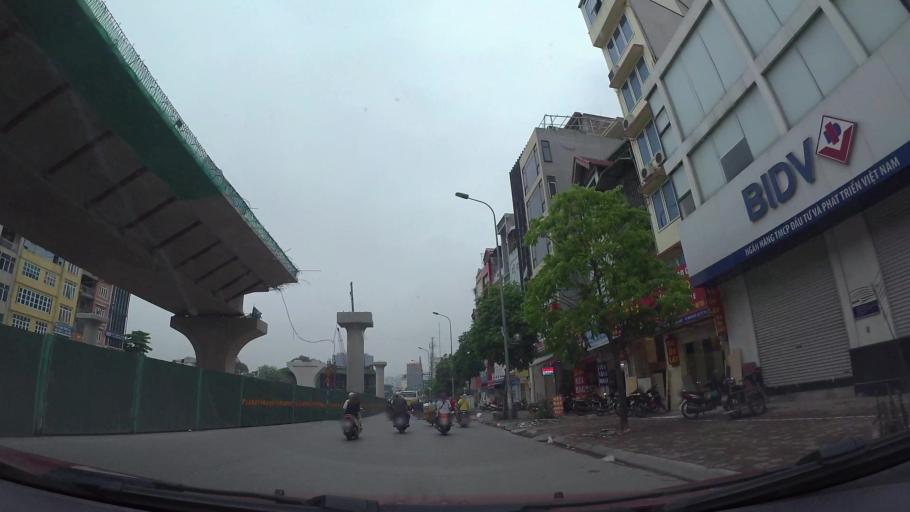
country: VN
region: Ha Noi
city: Hai BaTrung
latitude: 20.9990
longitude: 105.8372
